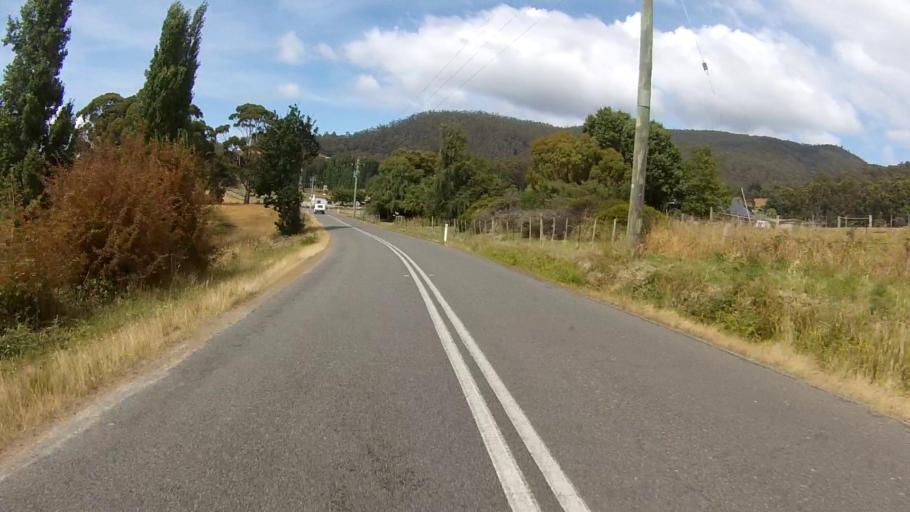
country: AU
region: Tasmania
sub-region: Kingborough
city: Kettering
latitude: -43.2135
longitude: 147.2552
